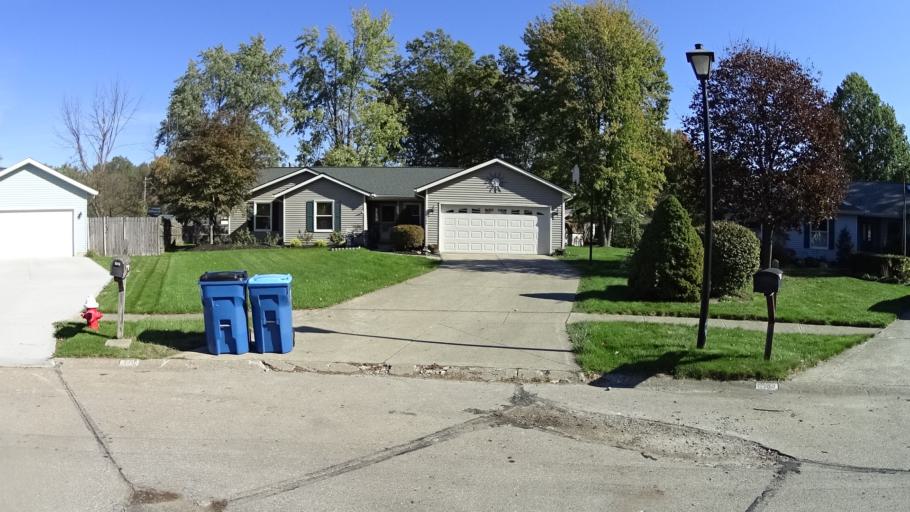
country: US
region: Ohio
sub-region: Lorain County
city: Lorain
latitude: 41.4139
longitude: -82.1715
